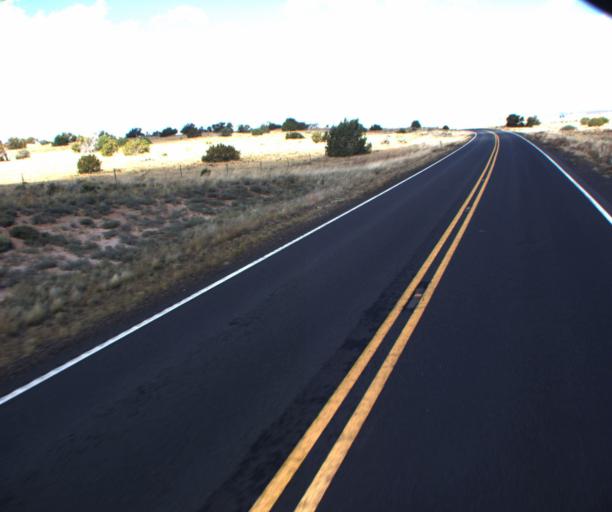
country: US
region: Arizona
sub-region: Apache County
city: Houck
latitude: 35.0047
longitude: -109.2285
